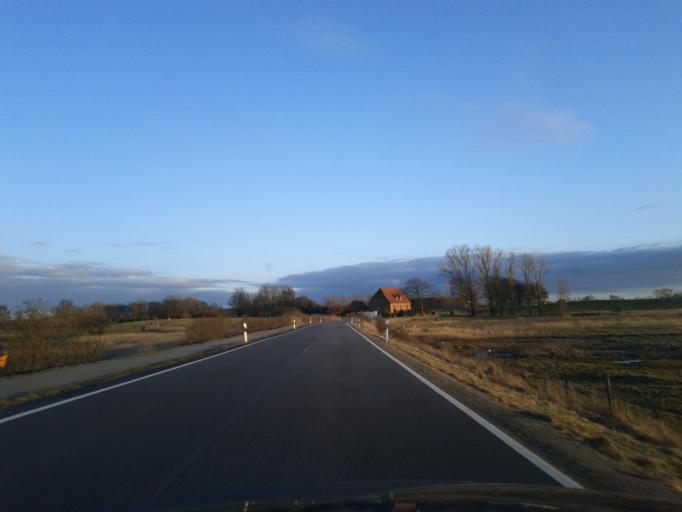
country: DE
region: Mecklenburg-Vorpommern
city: Blowatz
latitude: 53.9686
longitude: 11.4846
